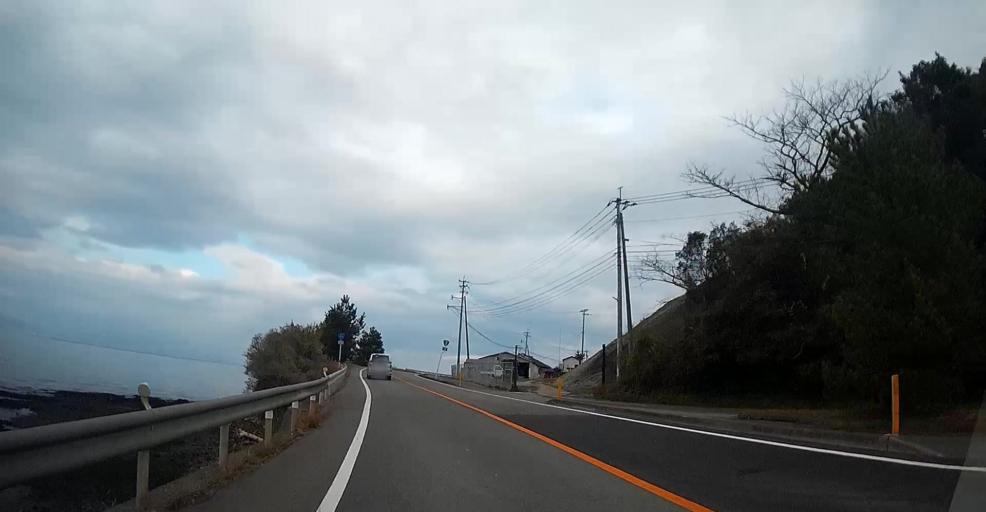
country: JP
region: Kumamoto
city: Hondo
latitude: 32.4860
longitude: 130.2841
